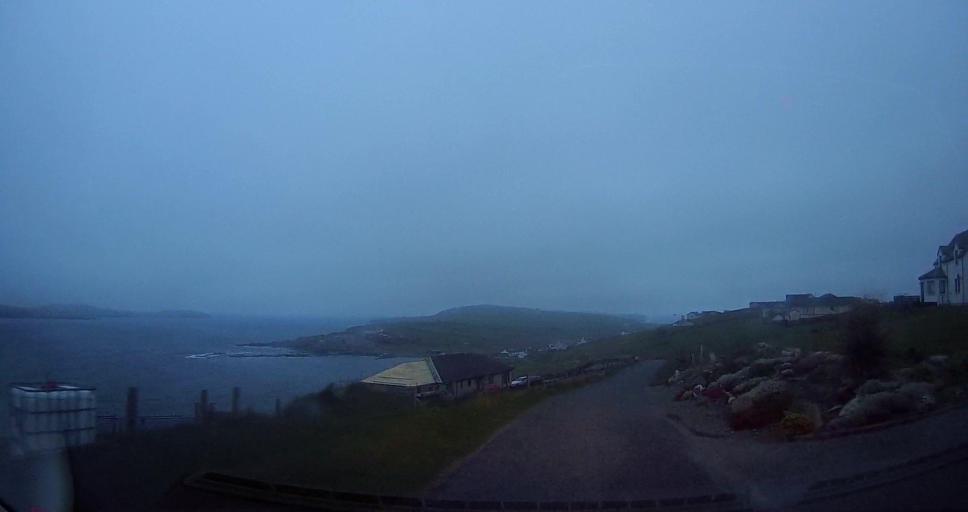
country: GB
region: Scotland
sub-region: Shetland Islands
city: Sandwick
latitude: 60.0116
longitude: -1.2267
